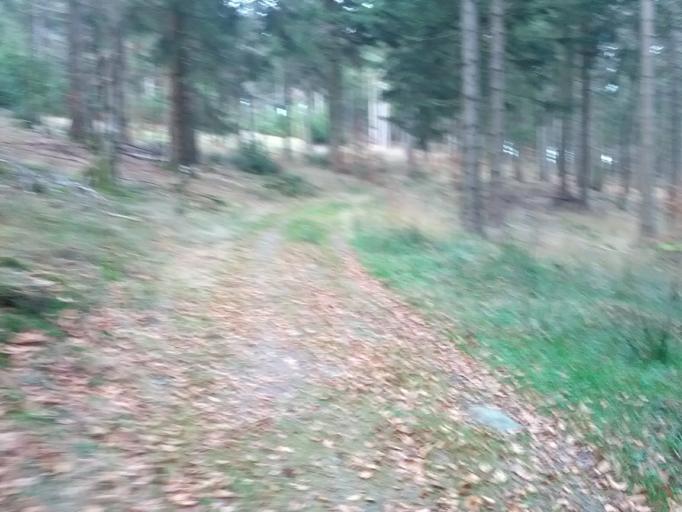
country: DE
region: Thuringia
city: Steinbach
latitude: 50.8569
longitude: 10.4071
